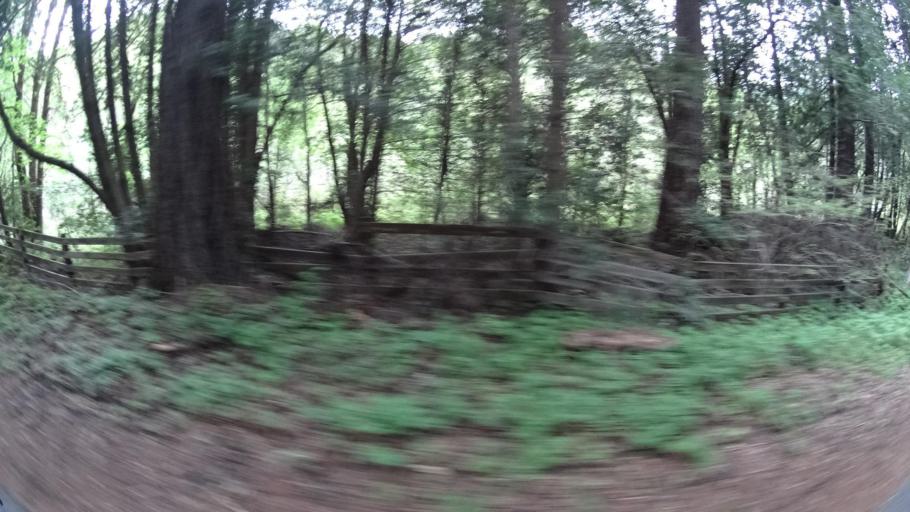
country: US
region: California
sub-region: Humboldt County
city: Blue Lake
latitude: 40.9628
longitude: -123.8402
